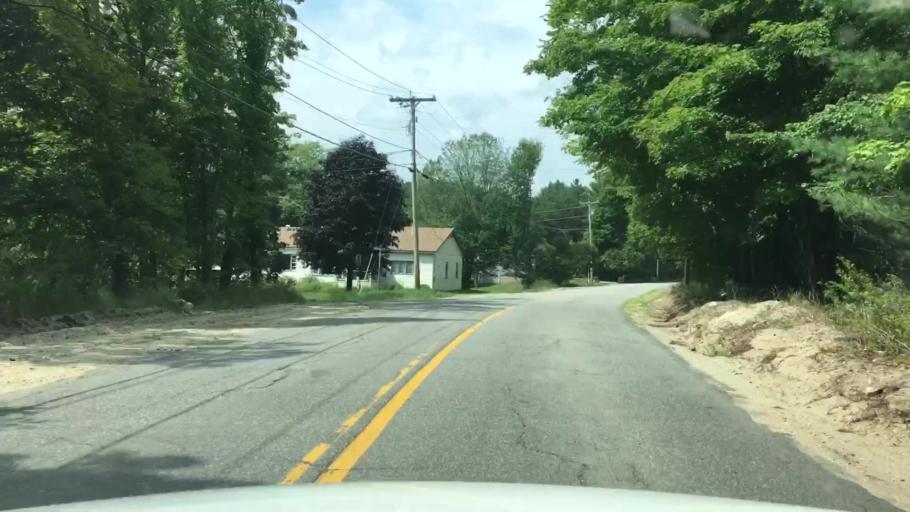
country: US
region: Maine
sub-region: Oxford County
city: Rumford
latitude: 44.5313
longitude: -70.6652
